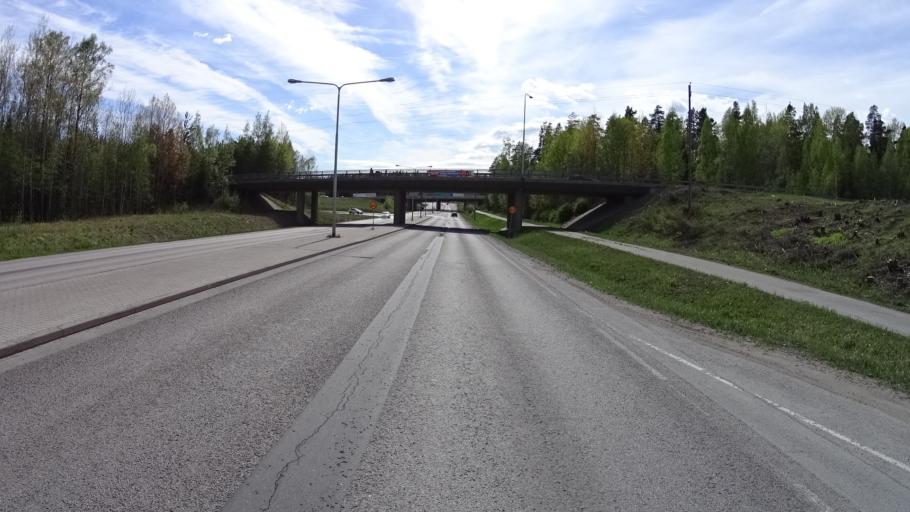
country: FI
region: Uusimaa
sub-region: Helsinki
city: Kilo
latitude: 60.3100
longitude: 24.8497
